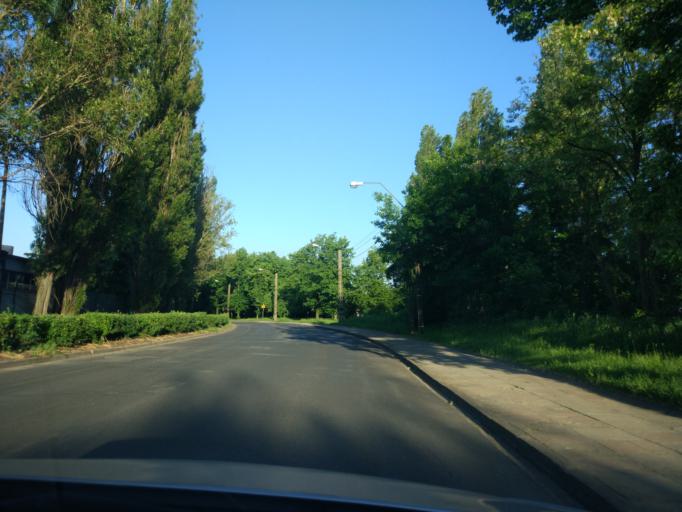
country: PL
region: Lodz Voivodeship
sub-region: Powiat kutnowski
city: Kutno
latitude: 52.2255
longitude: 19.3561
